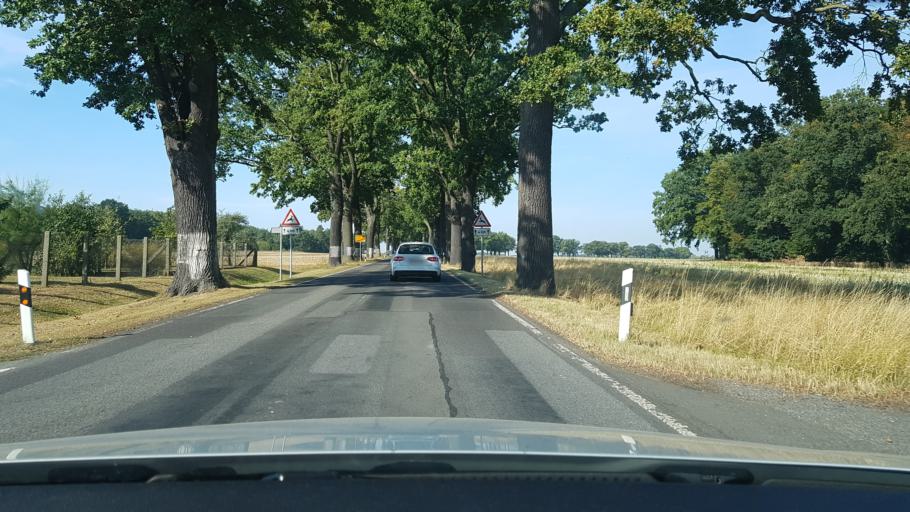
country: DE
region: Brandenburg
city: Beeskow
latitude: 52.1565
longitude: 14.3108
